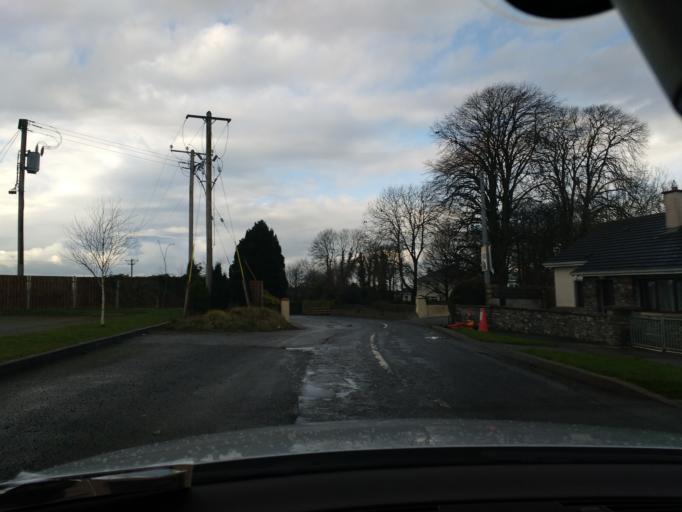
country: IE
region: Leinster
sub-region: Laois
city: Rathdowney
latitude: 52.6770
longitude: -7.6045
